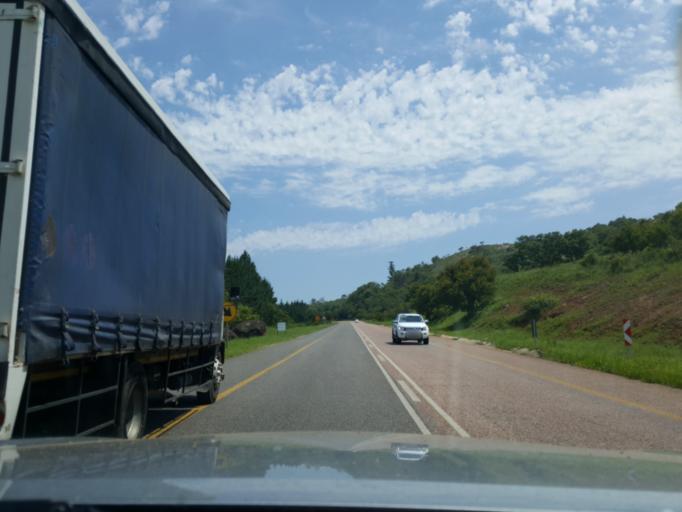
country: ZA
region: Mpumalanga
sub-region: Ehlanzeni District
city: White River
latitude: -25.1924
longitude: 31.0051
